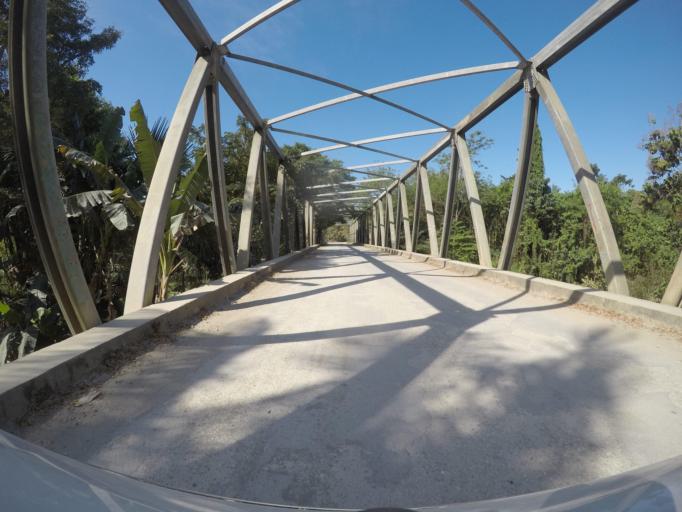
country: TL
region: Viqueque
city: Viqueque
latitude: -8.8334
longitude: 126.5195
